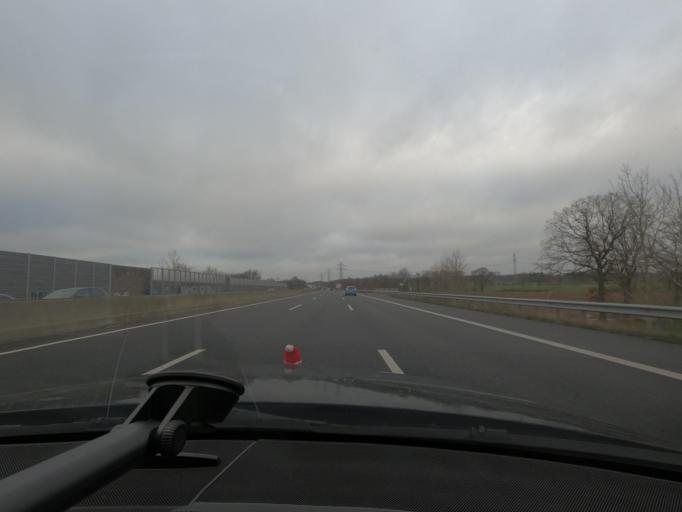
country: DE
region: Schleswig-Holstein
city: Ellerau
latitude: 53.7630
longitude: 9.9490
